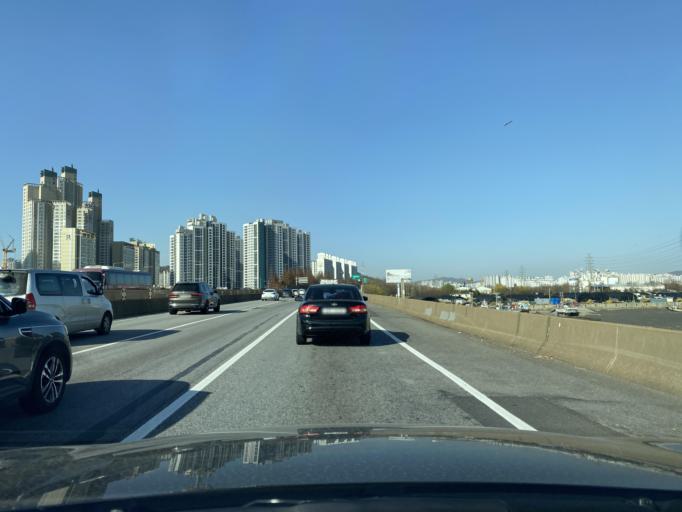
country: KR
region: Incheon
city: Incheon
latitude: 37.3981
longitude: 126.7423
